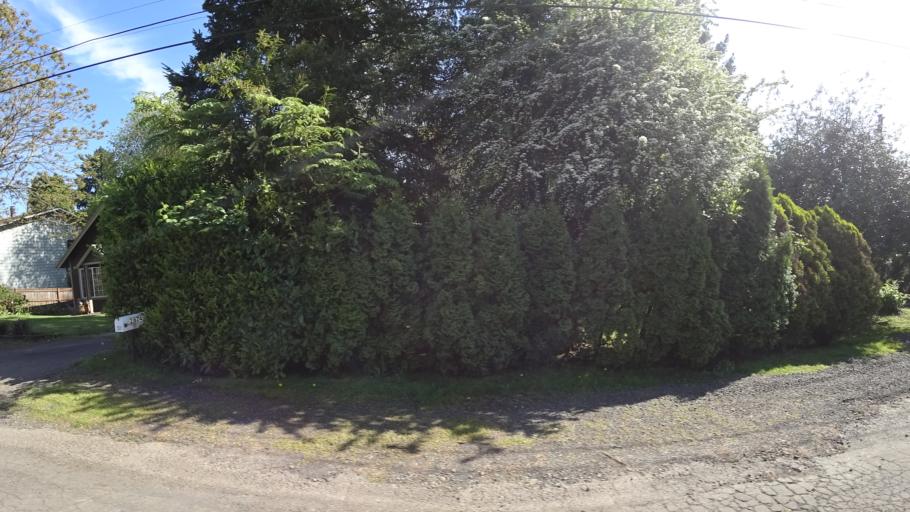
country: US
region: Oregon
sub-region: Clackamas County
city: Milwaukie
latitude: 45.4561
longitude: -122.6336
